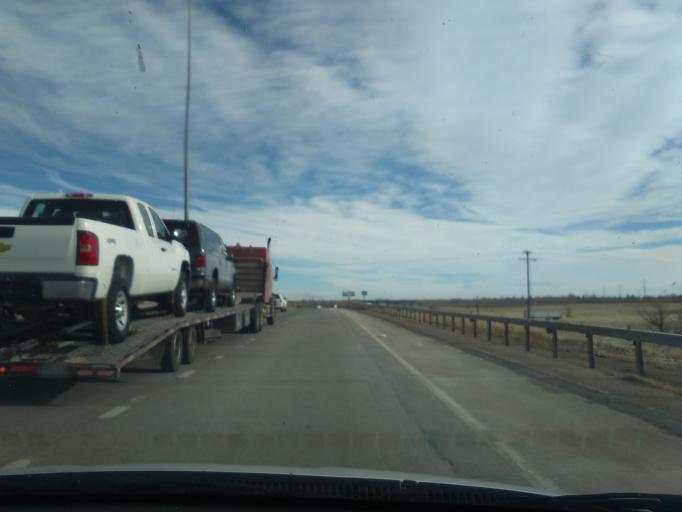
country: US
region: Wyoming
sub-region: Laramie County
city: Cheyenne
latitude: 41.1151
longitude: -104.8449
